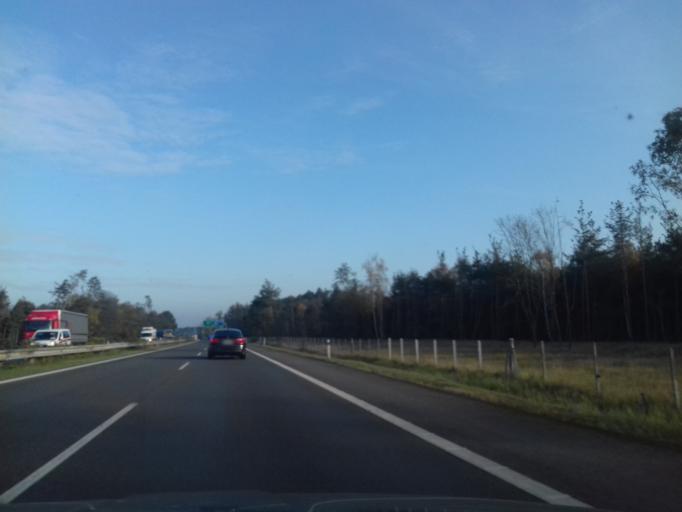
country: SK
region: Bratislavsky
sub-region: Okres Malacky
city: Malacky
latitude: 48.4126
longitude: 17.0371
